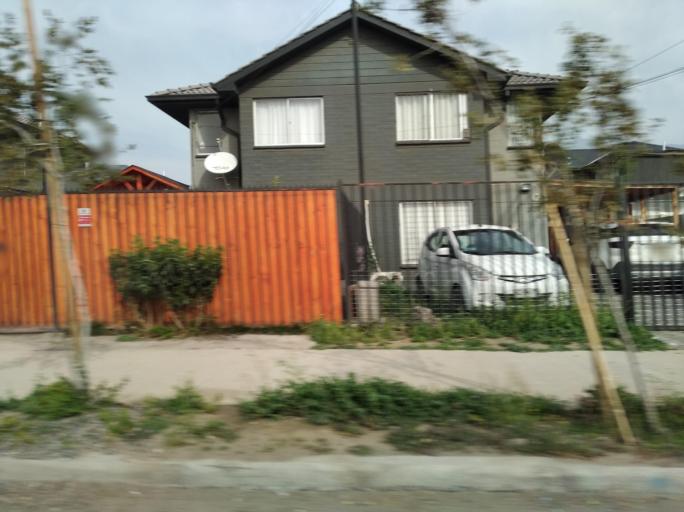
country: CL
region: Santiago Metropolitan
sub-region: Provincia de Chacabuco
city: Lampa
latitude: -33.3001
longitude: -70.8786
